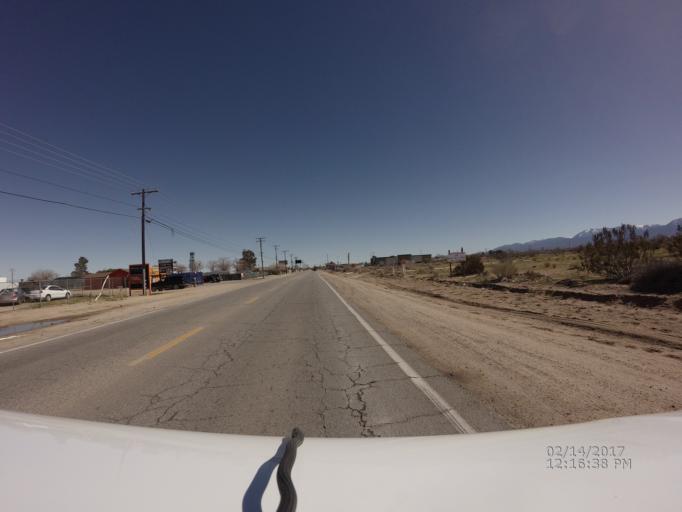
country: US
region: California
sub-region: Los Angeles County
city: Littlerock
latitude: 34.5797
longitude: -117.9730
